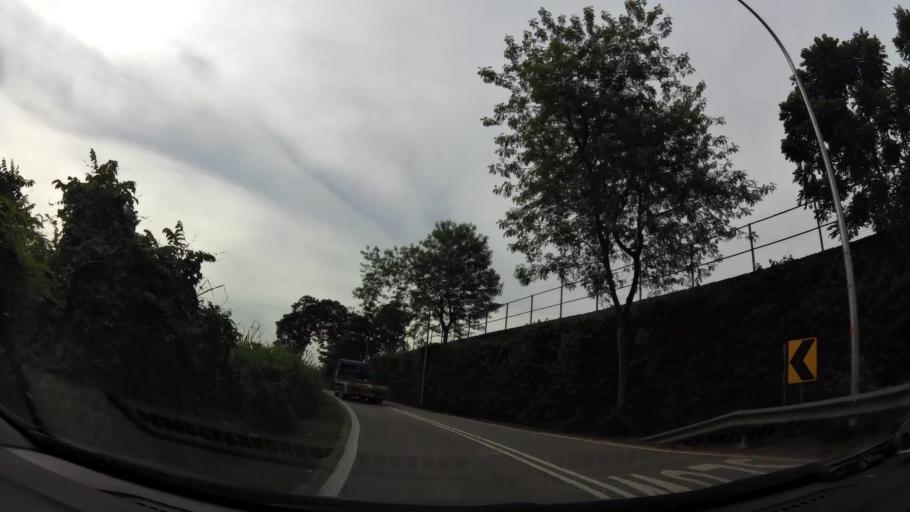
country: MY
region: Johor
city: Johor Bahru
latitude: 1.4183
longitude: 103.7120
